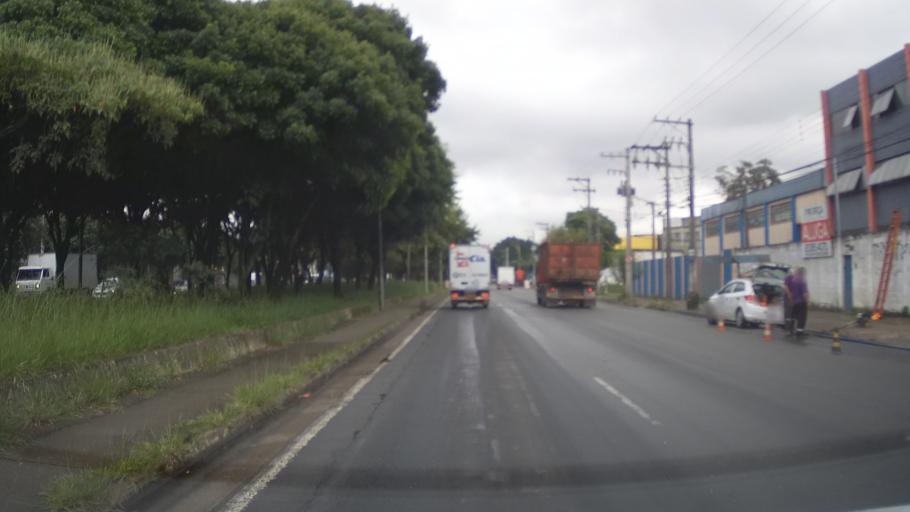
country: BR
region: Sao Paulo
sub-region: Guarulhos
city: Guarulhos
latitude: -23.4739
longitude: -46.4671
